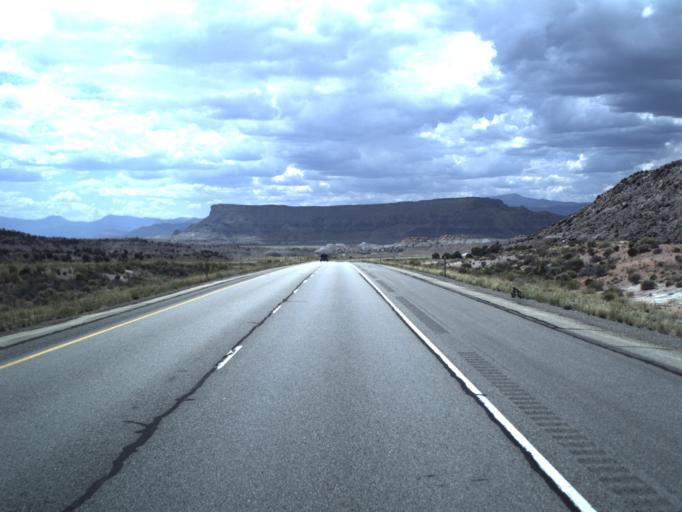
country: US
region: Utah
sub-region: Emery County
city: Ferron
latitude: 38.8224
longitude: -111.1497
